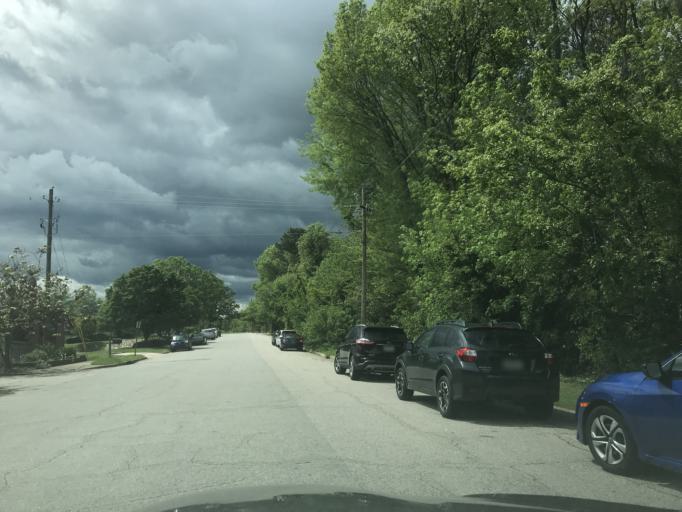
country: US
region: North Carolina
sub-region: Wake County
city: West Raleigh
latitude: 35.7950
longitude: -78.7000
